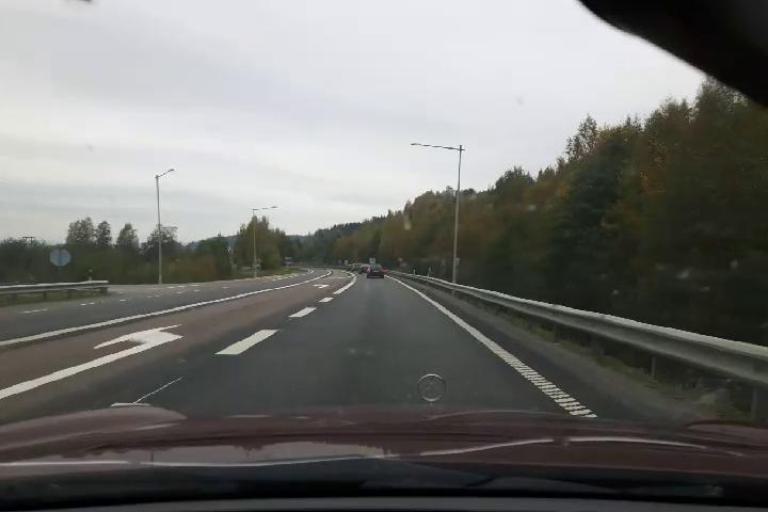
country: SE
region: Vaesternorrland
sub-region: OErnskoeldsviks Kommun
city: Ornskoldsvik
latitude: 63.2978
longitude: 18.6549
